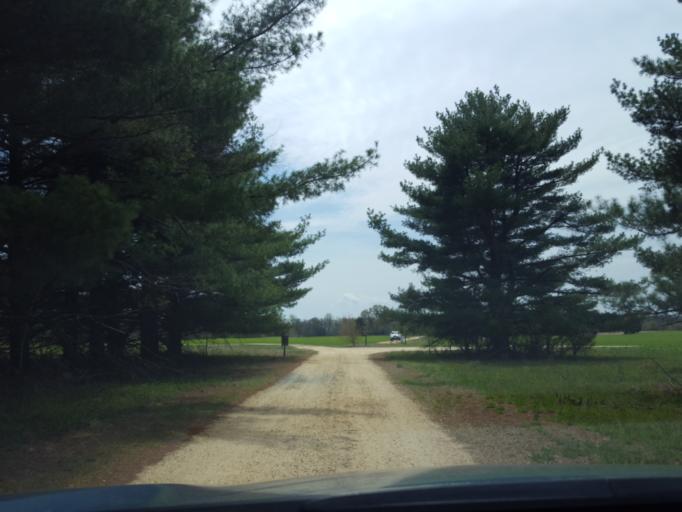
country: US
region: Maryland
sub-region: Calvert County
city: Dunkirk
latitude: 38.7334
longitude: -76.7020
